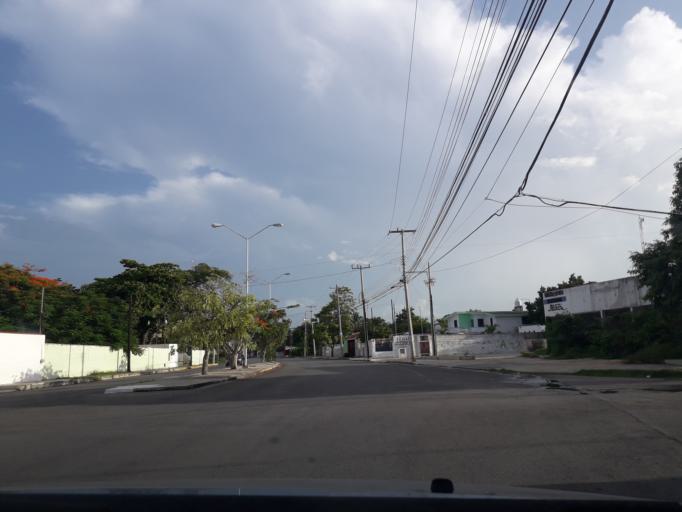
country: MX
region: Yucatan
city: Merida
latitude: 21.0213
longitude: -89.6314
